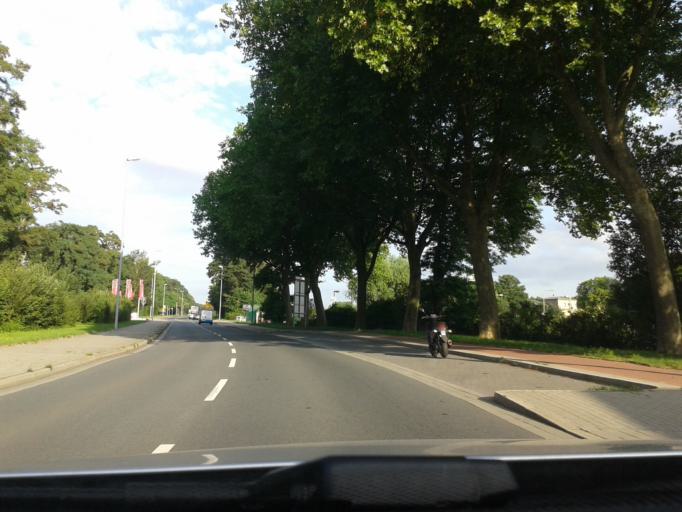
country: DE
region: North Rhine-Westphalia
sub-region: Regierungsbezirk Dusseldorf
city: Muelheim (Ruhr)
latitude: 51.4406
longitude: 6.8305
